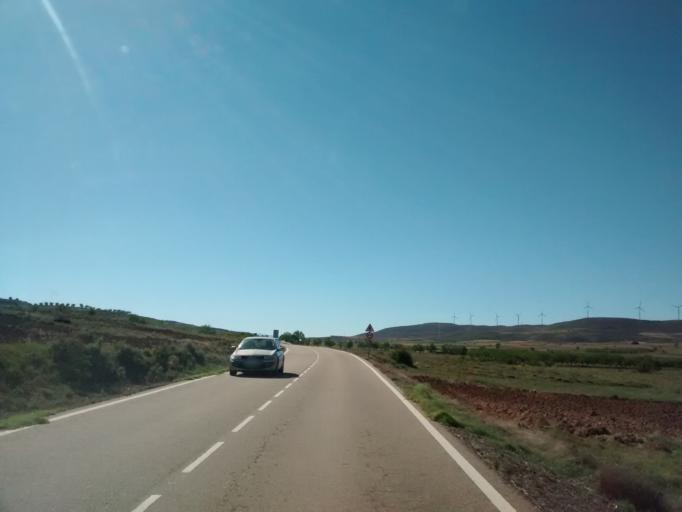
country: ES
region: Aragon
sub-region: Provincia de Zaragoza
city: Trasmoz
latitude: 41.8434
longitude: -1.7203
